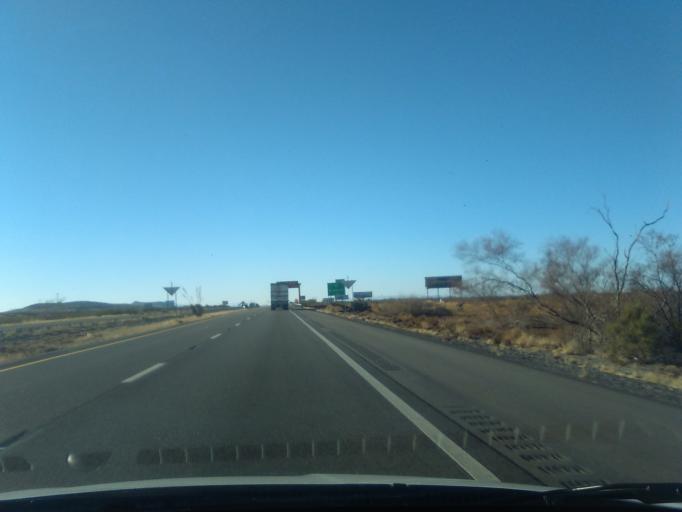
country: US
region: New Mexico
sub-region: Hidalgo County
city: Lordsburg
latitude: 32.3452
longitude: -108.7199
